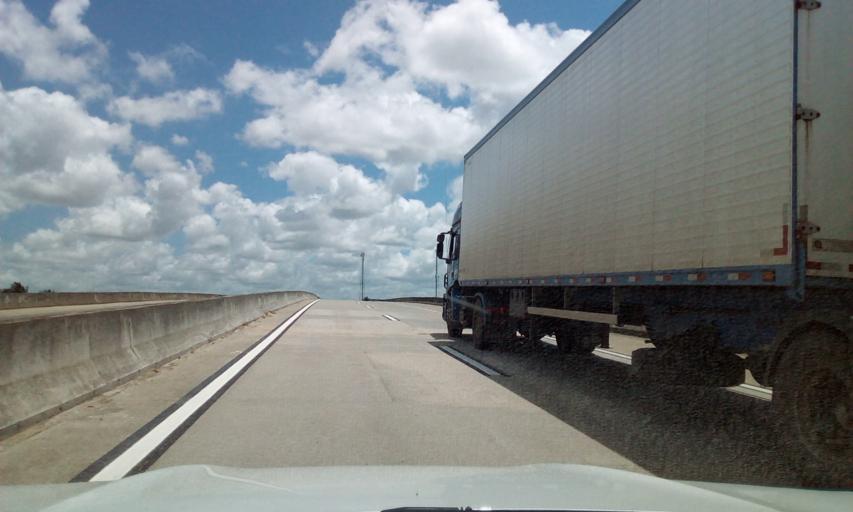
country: BR
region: Alagoas
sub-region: Campo Alegre
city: Campo Alegre
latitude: -9.9063
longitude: -36.3522
